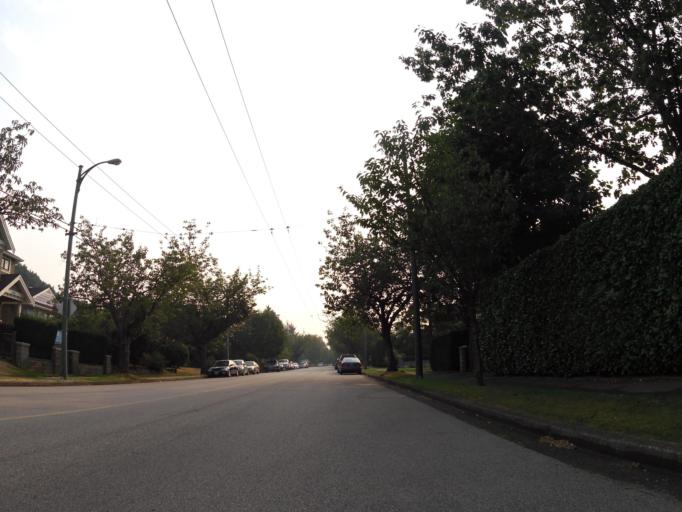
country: CA
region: British Columbia
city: Richmond
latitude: 49.2132
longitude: -123.1460
